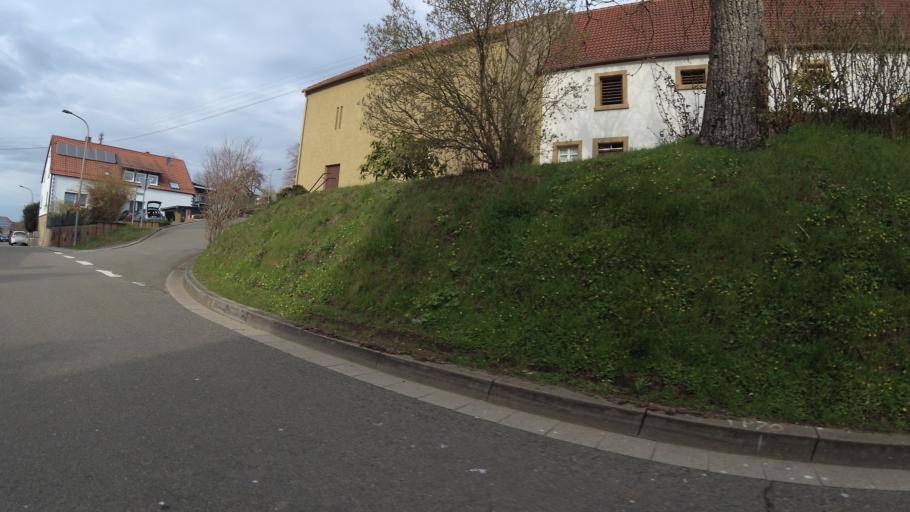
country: DE
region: Rheinland-Pfalz
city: Huffler
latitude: 49.4965
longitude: 7.3919
